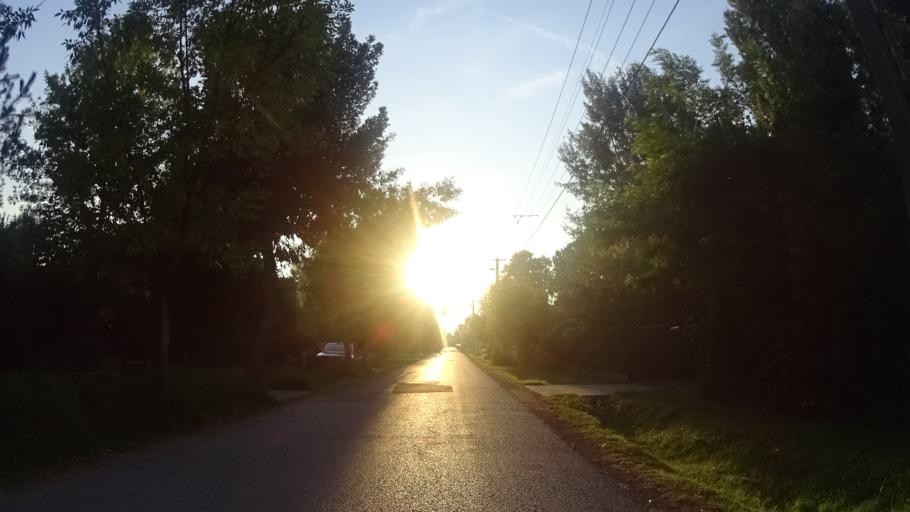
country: HU
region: Somogy
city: Zamardi
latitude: 46.8861
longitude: 17.9494
